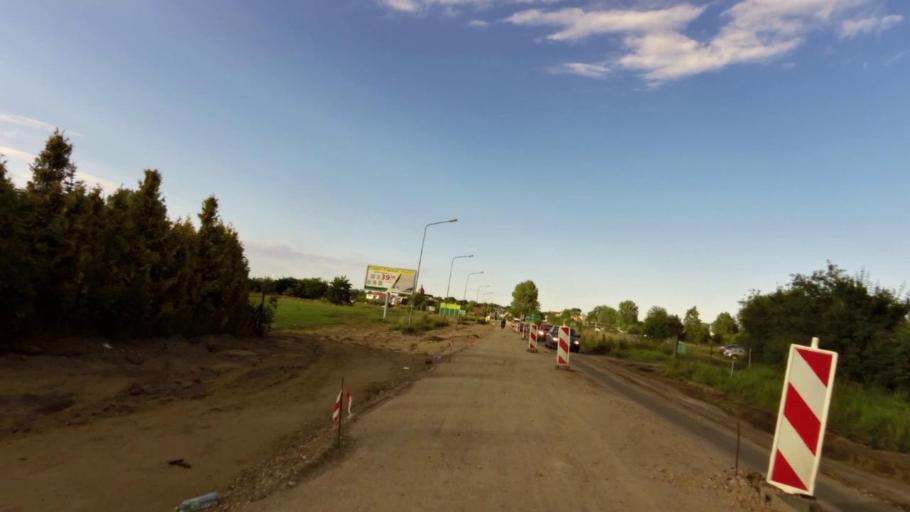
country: PL
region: West Pomeranian Voivodeship
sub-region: Powiat slawienski
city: Darlowo
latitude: 54.4126
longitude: 16.3979
